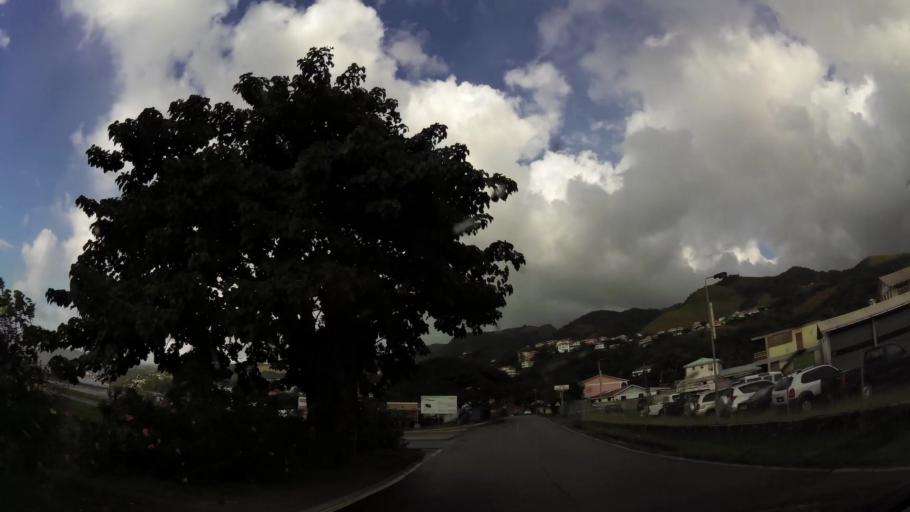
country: DM
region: Saint George
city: Roseau
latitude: 15.3318
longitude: -61.3916
